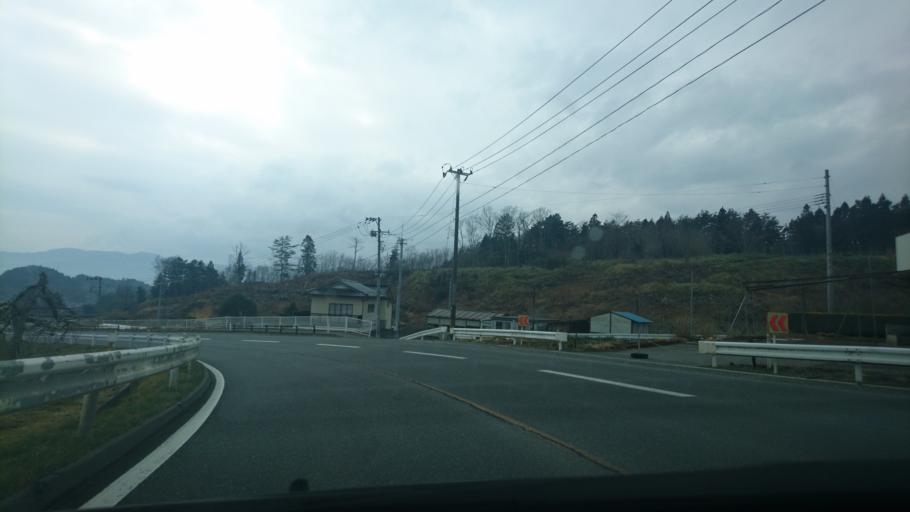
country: JP
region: Iwate
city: Ofunato
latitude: 39.0237
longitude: 141.6741
